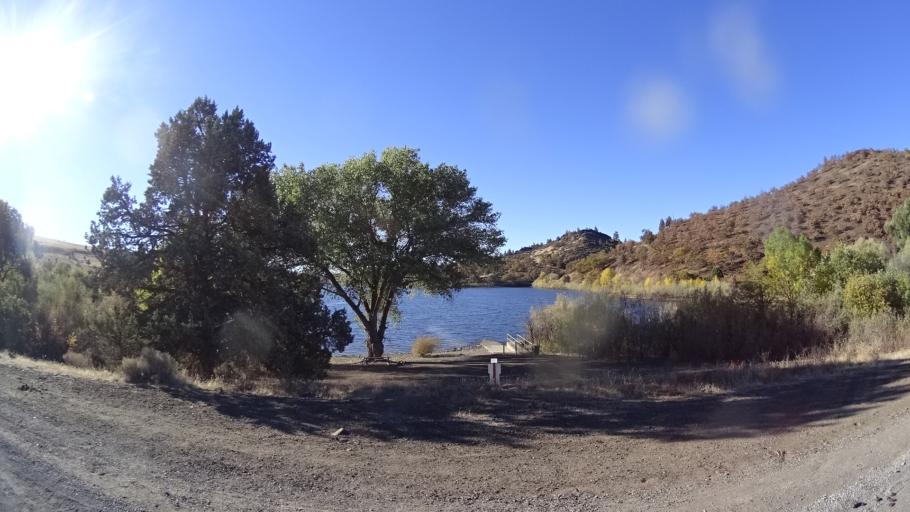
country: US
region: California
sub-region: Siskiyou County
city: Montague
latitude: 41.9742
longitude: -122.4374
